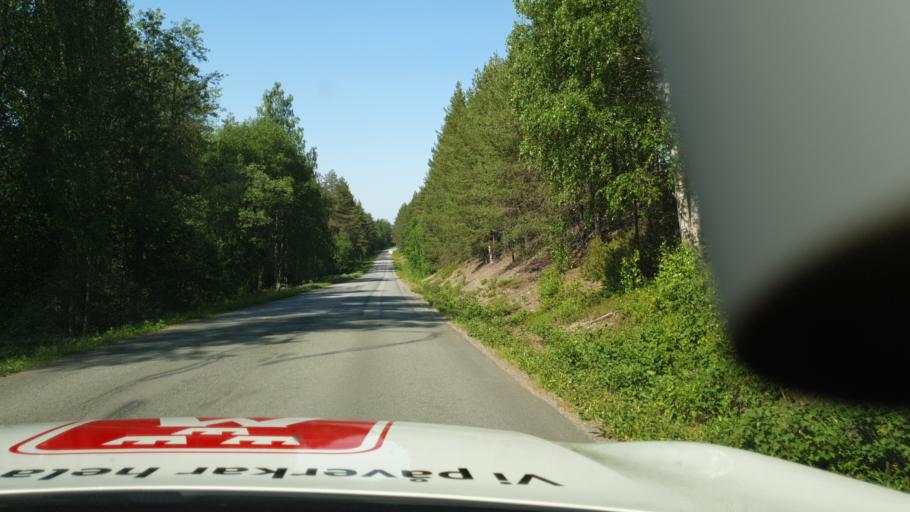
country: SE
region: Vaesterbotten
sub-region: Skelleftea Kommun
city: Langsele
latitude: 64.9417
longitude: 19.9693
